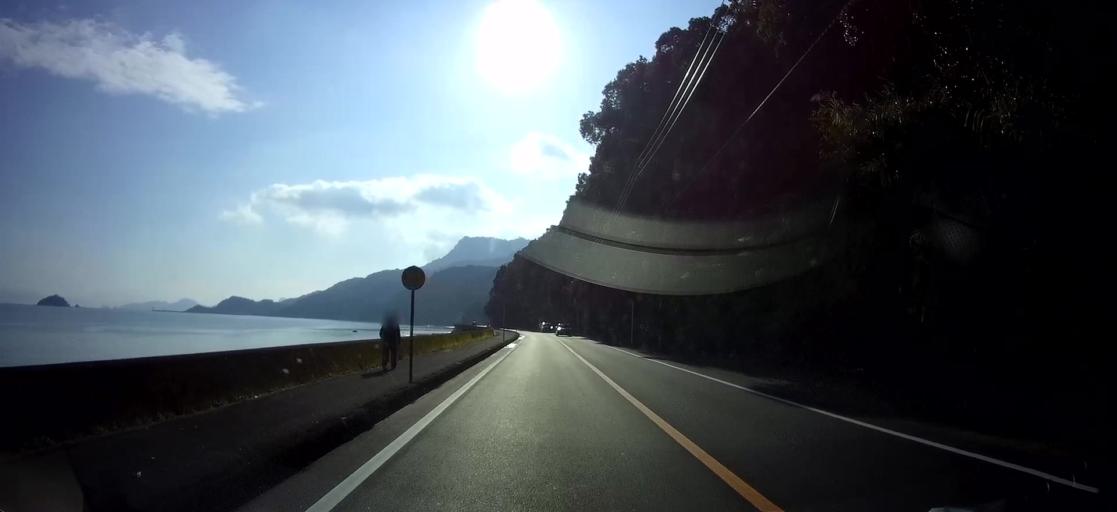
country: JP
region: Kumamoto
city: Yatsushiro
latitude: 32.4921
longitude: 130.4424
